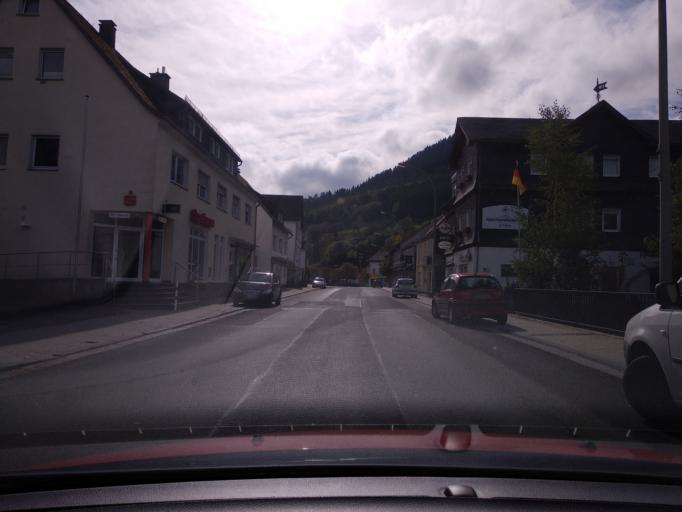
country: DE
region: North Rhine-Westphalia
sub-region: Regierungsbezirk Arnsberg
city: Bestwig
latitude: 51.3107
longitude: 8.4025
